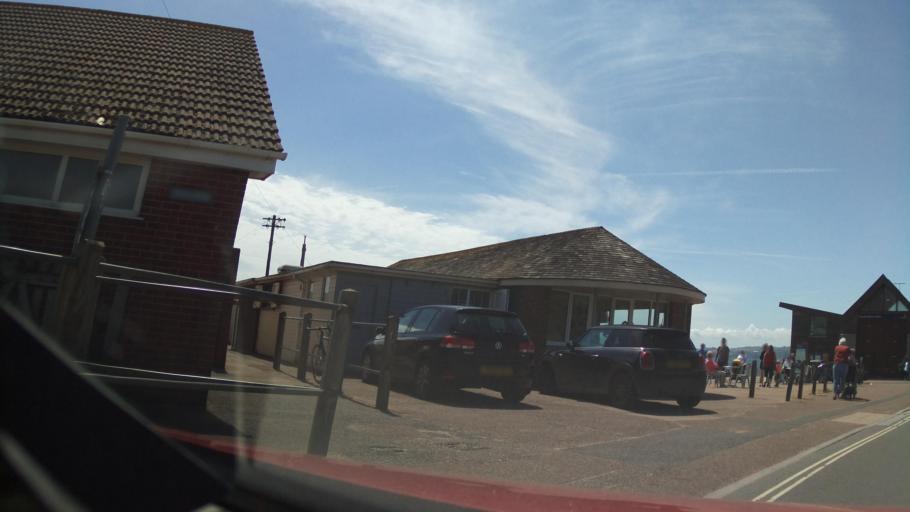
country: GB
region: England
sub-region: Devon
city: Exmouth
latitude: 50.6111
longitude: -3.3979
